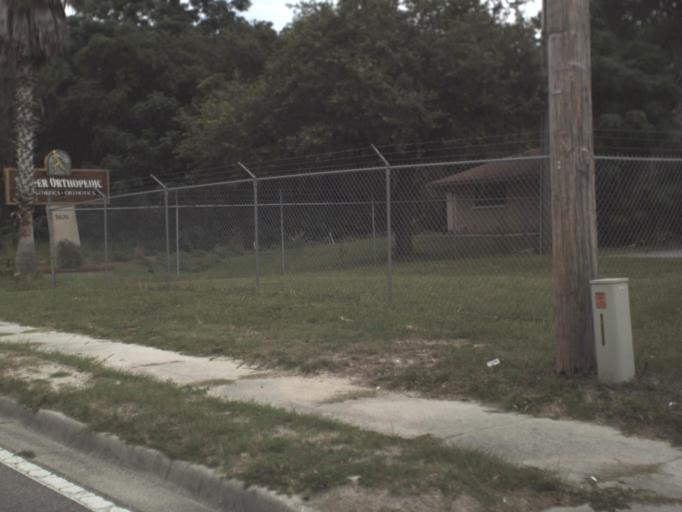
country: US
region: Florida
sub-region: Citrus County
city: Lecanto
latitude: 28.8790
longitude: -82.5291
